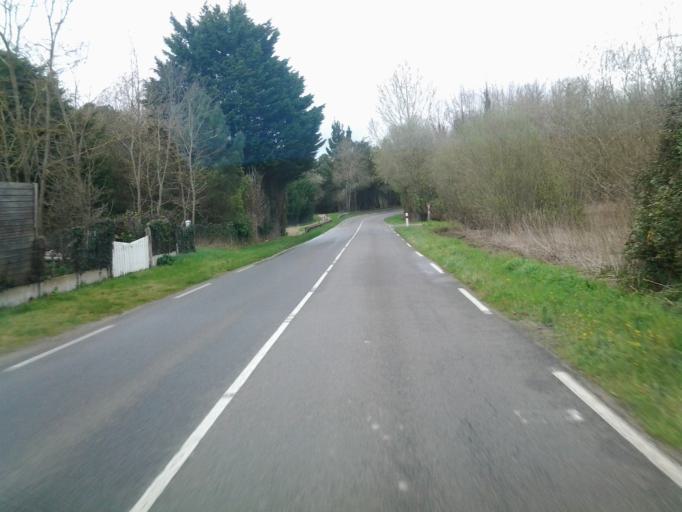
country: FR
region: Pays de la Loire
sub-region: Departement de la Vendee
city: La Tranche-sur-Mer
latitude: 46.3794
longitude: -1.4654
